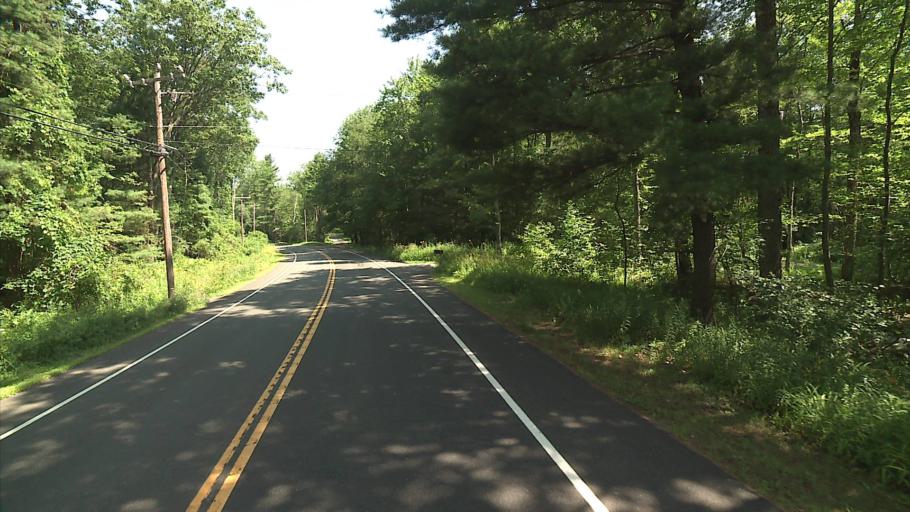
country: US
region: Massachusetts
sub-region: Berkshire County
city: New Marlborough
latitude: 42.0323
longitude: -73.2070
